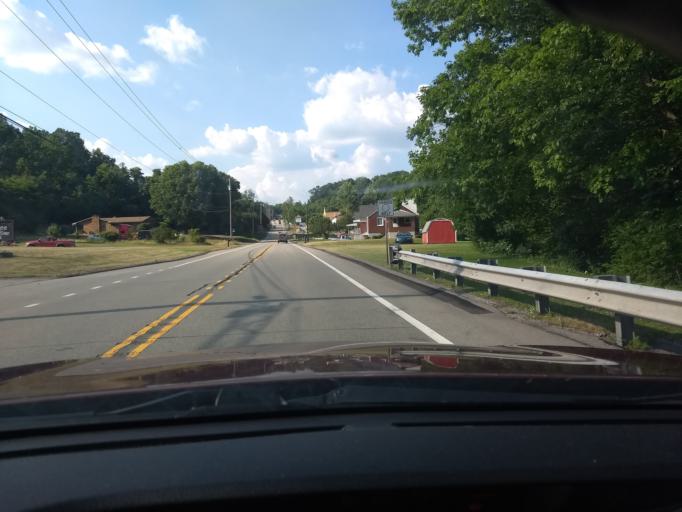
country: US
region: Pennsylvania
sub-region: Allegheny County
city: North Versailles
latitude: 40.3594
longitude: -79.7859
